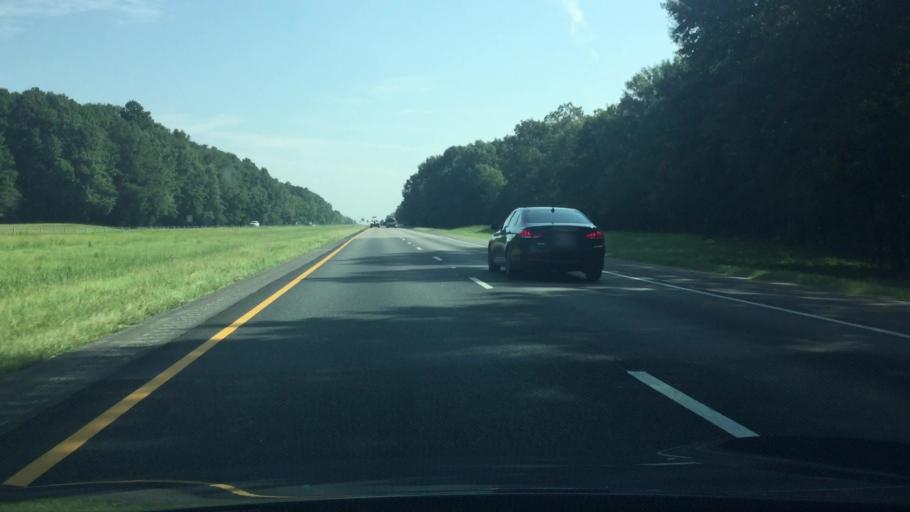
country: US
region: Alabama
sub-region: Montgomery County
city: Montgomery
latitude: 32.2385
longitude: -86.3774
